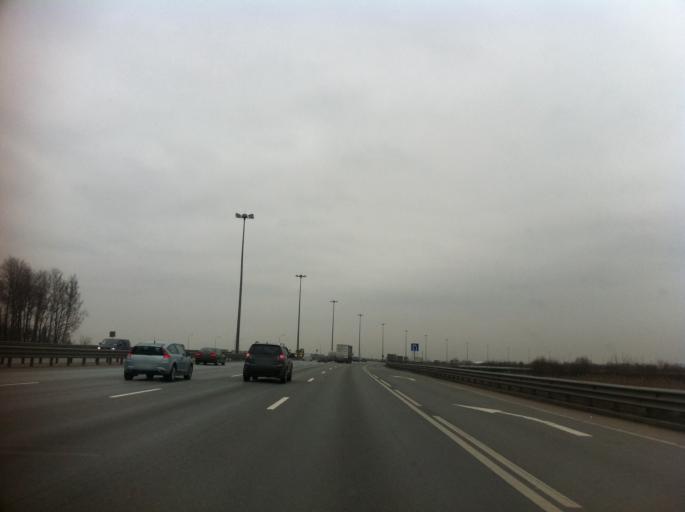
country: RU
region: Leningrad
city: Rybatskoye
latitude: 59.8751
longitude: 30.5308
